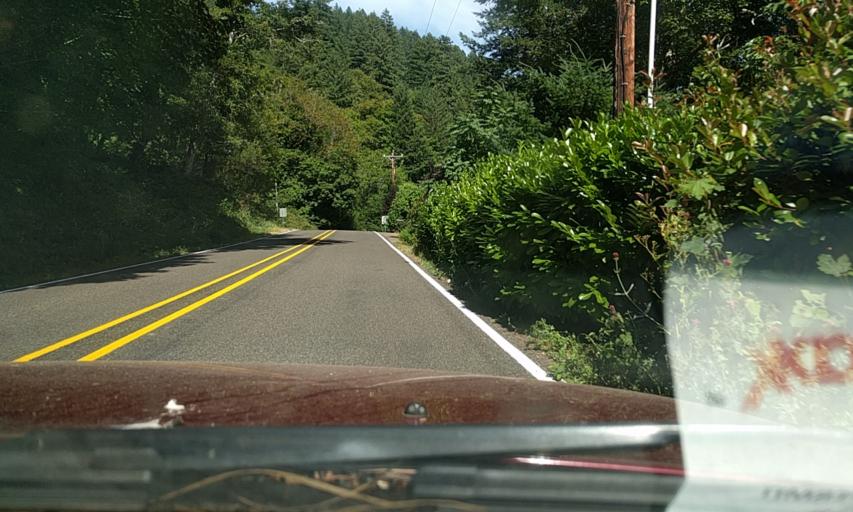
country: US
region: Oregon
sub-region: Lane County
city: Florence
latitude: 44.0423
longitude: -123.8699
